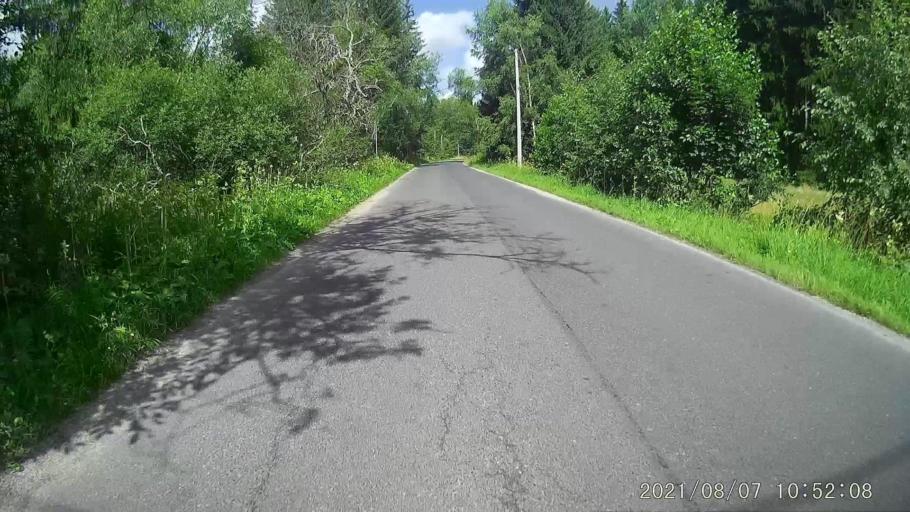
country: CZ
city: Rokytnice v Orlickych Horach
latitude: 50.2839
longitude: 16.4718
